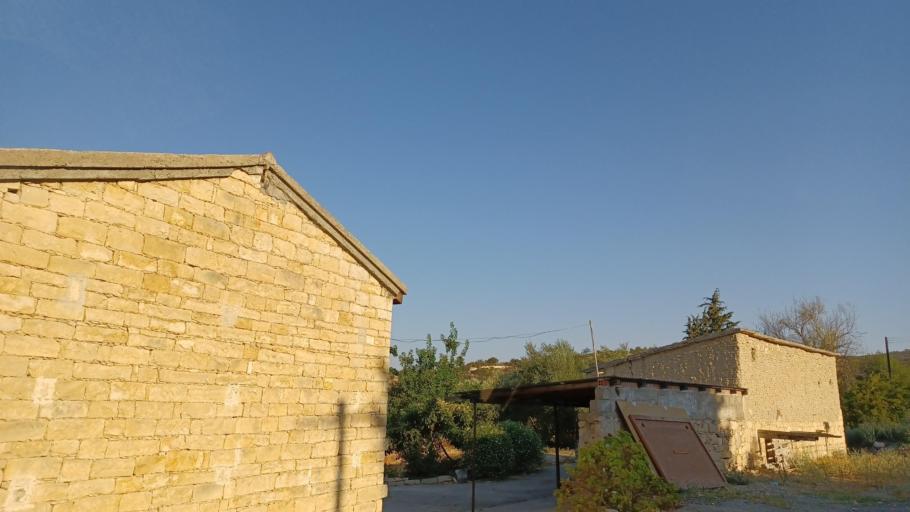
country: CY
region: Limassol
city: Pissouri
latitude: 34.7096
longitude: 32.6817
